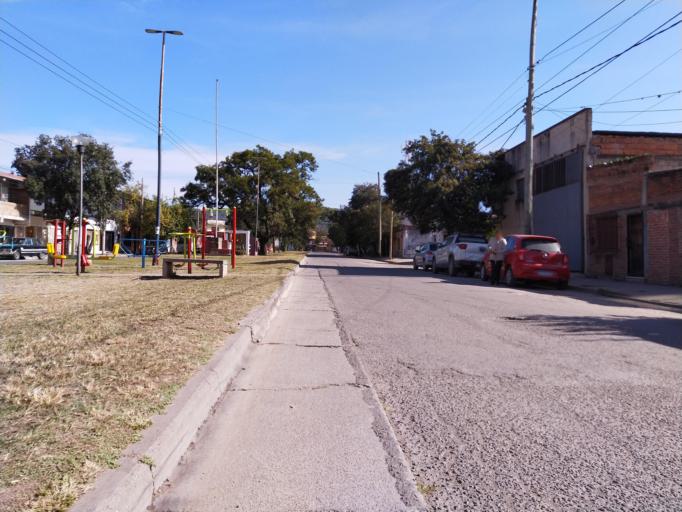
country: AR
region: Jujuy
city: San Salvador de Jujuy
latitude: -24.2006
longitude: -65.2827
